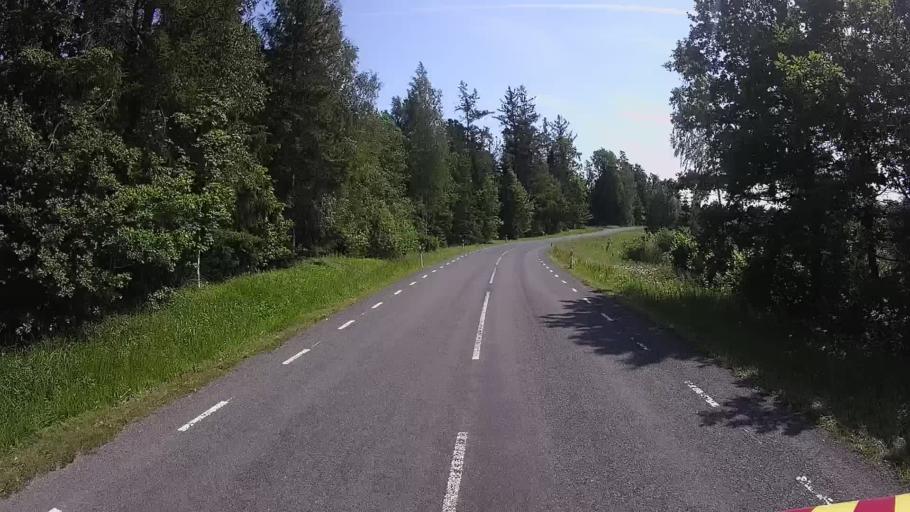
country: EE
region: Viljandimaa
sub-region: Karksi vald
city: Karksi-Nuia
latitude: 58.0792
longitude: 25.5607
